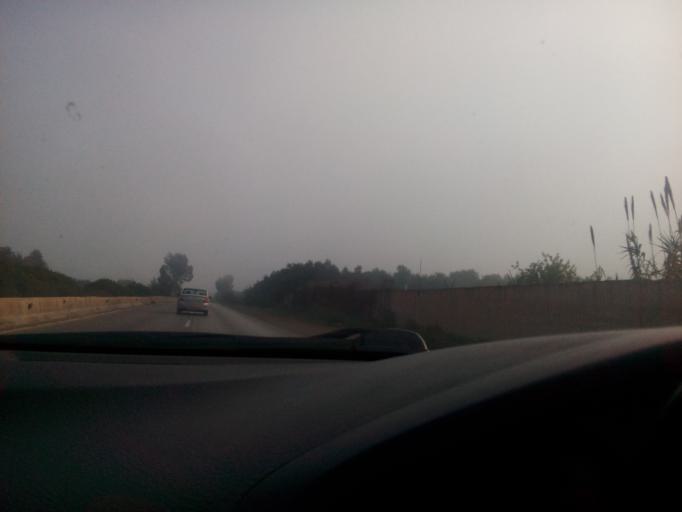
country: DZ
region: Oran
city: Bou Tlelis
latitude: 35.5926
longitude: -0.7933
